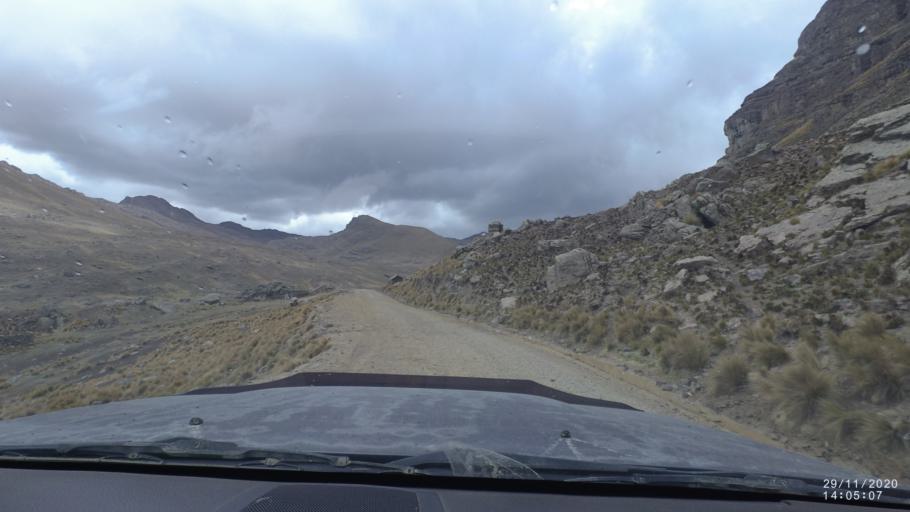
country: BO
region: Cochabamba
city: Sipe Sipe
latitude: -17.2047
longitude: -66.3776
